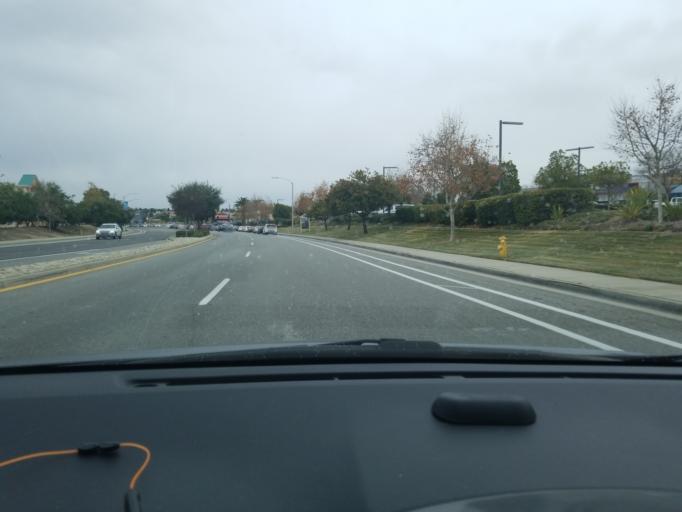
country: US
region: California
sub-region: Riverside County
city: Murrieta Hot Springs
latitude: 33.5293
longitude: -117.1498
